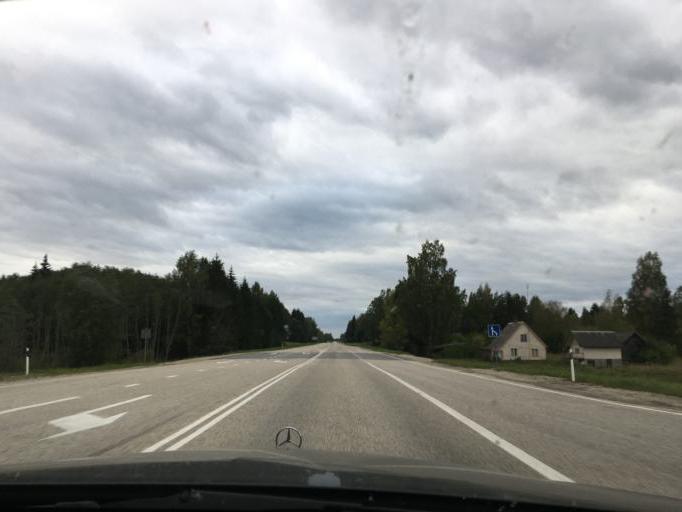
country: RU
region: Pskov
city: Pechory
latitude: 57.6361
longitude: 27.3415
